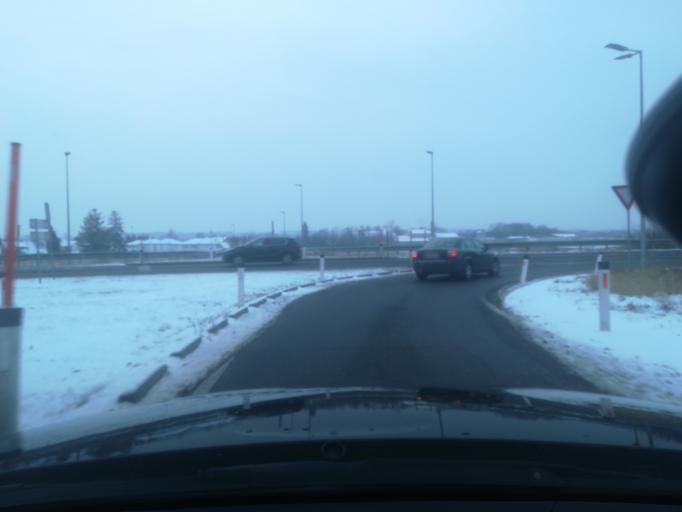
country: AT
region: Upper Austria
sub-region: Wels-Land
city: Marchtrenk
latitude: 48.1897
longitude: 14.1046
